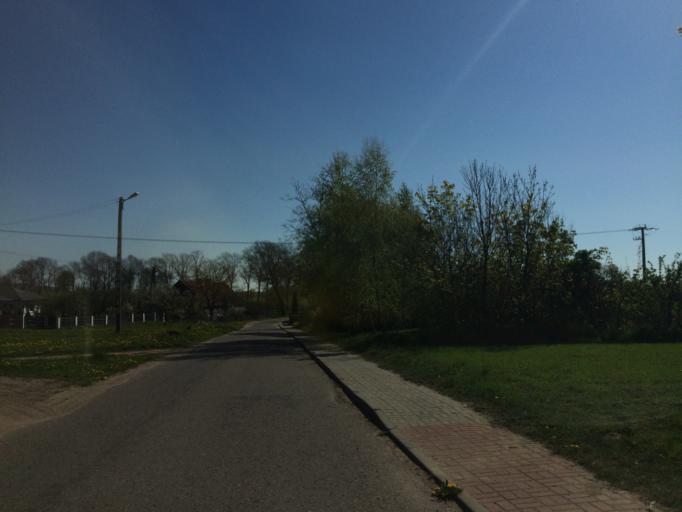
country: PL
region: Warmian-Masurian Voivodeship
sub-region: Powiat dzialdowski
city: Rybno
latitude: 53.4600
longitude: 19.9549
